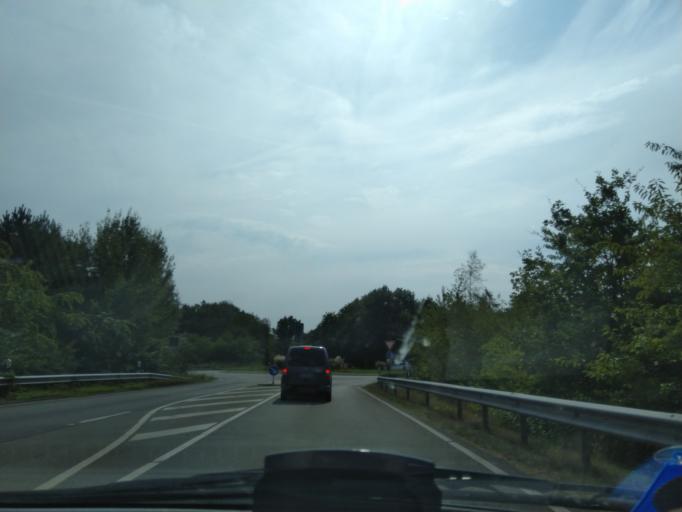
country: DE
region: Lower Saxony
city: Meppen
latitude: 52.7129
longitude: 7.2933
